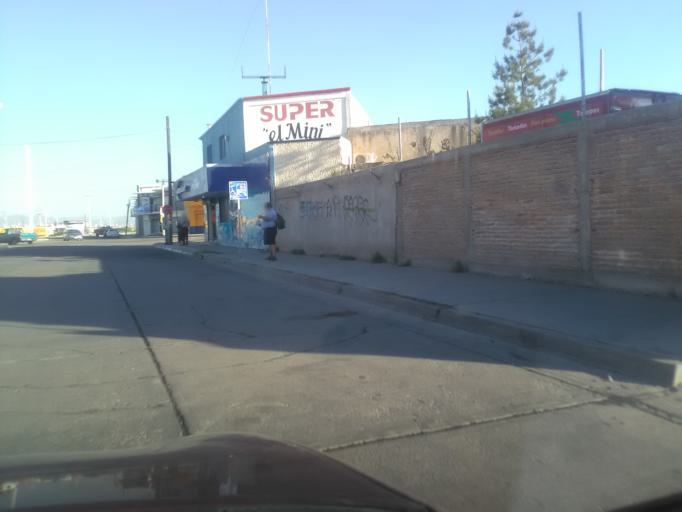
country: MX
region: Durango
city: Victoria de Durango
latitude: 24.0567
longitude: -104.5898
